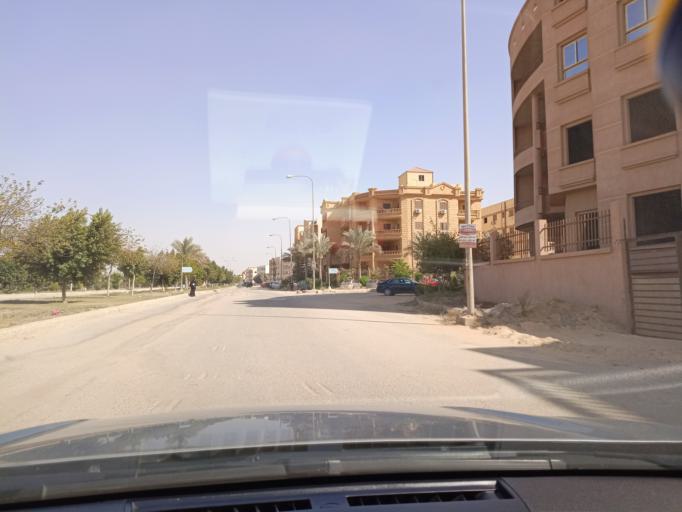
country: EG
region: Muhafazat al Qalyubiyah
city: Al Khankah
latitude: 30.2292
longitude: 31.4434
